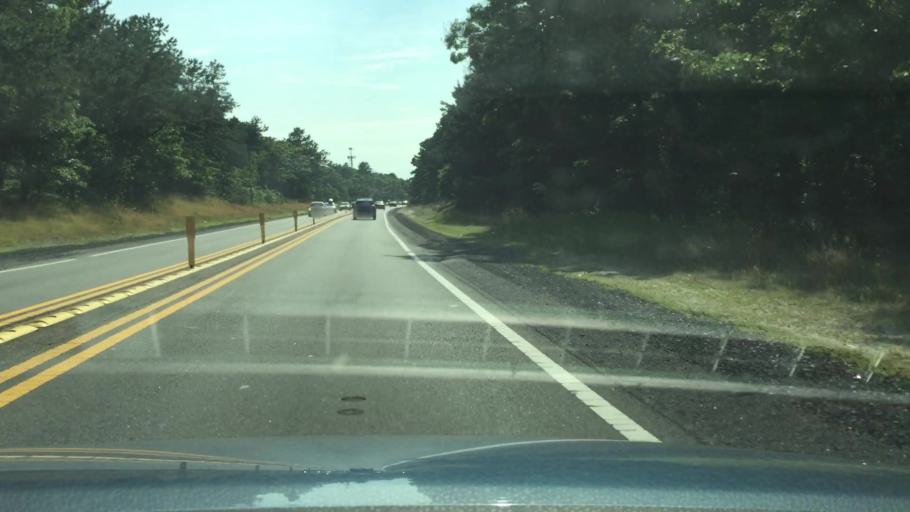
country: US
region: Massachusetts
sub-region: Barnstable County
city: Northwest Harwich
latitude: 41.7008
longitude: -70.0891
